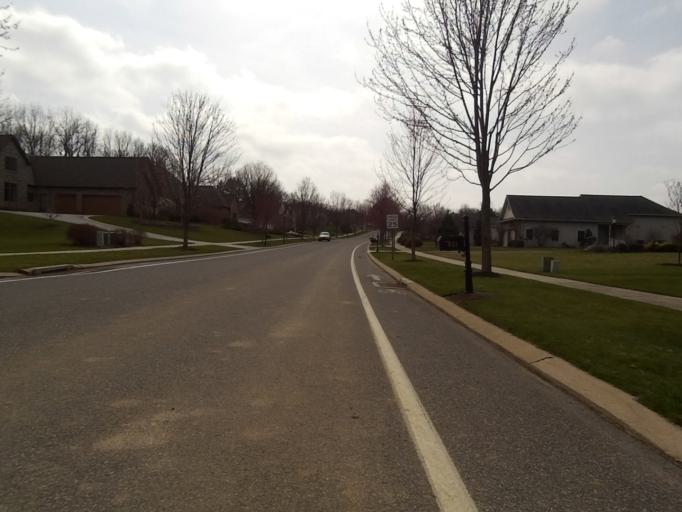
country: US
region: Pennsylvania
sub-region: Centre County
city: Boalsburg
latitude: 40.7874
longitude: -77.8108
